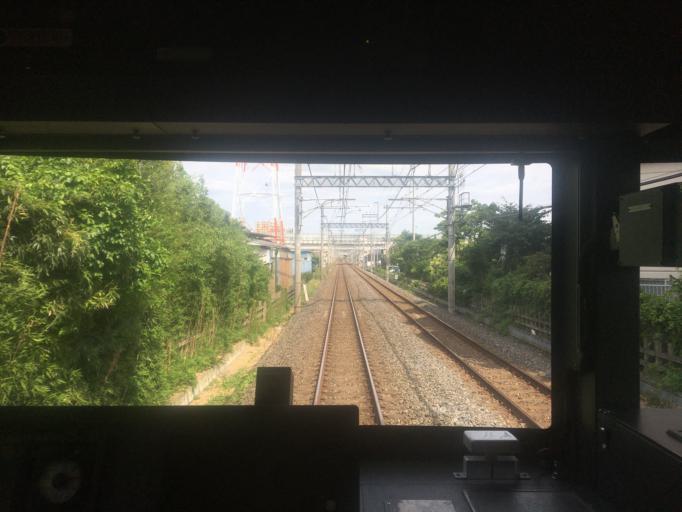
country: JP
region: Saitama
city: Sakado
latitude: 35.9431
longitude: 139.4159
